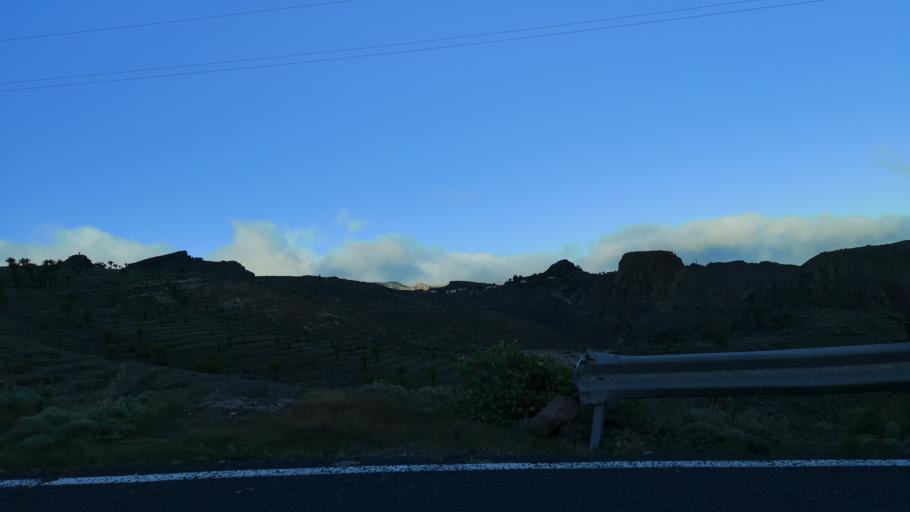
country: ES
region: Canary Islands
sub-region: Provincia de Santa Cruz de Tenerife
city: Alajero
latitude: 28.0507
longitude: -17.2318
